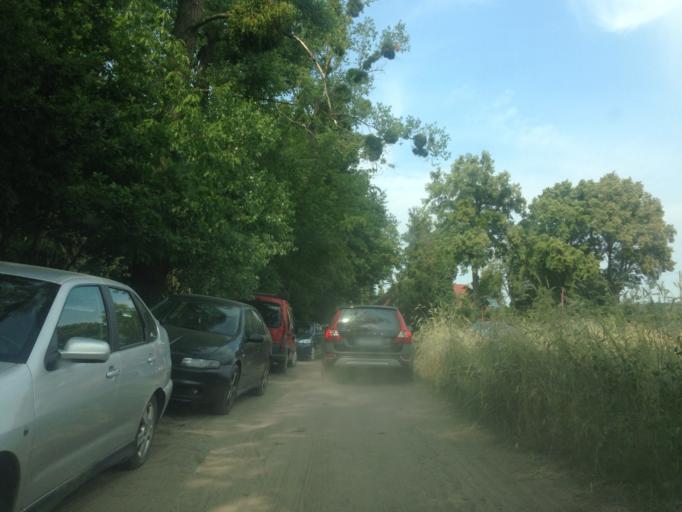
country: PL
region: Kujawsko-Pomorskie
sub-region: Powiat brodnicki
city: Bobrowo
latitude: 53.2583
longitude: 19.2979
